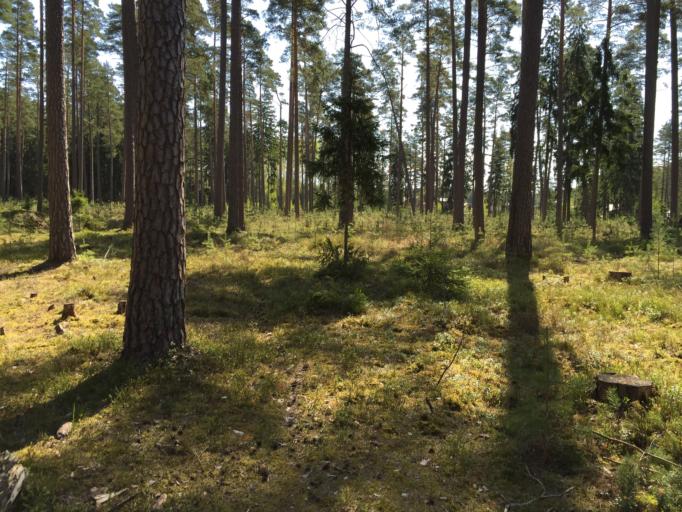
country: LV
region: Saulkrastu
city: Saulkrasti
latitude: 57.3158
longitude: 24.4383
